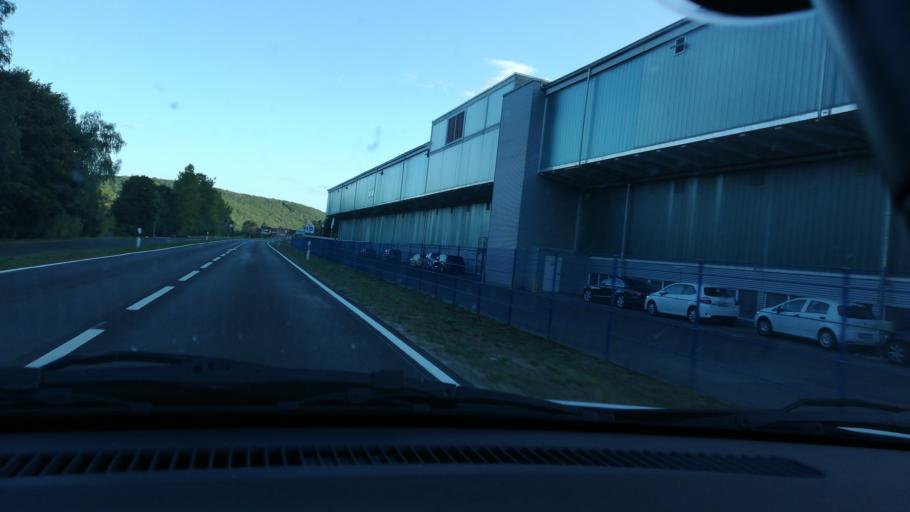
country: DE
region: Bavaria
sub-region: Regierungsbezirk Unterfranken
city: Hafenlohr
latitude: 49.8793
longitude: 9.6003
